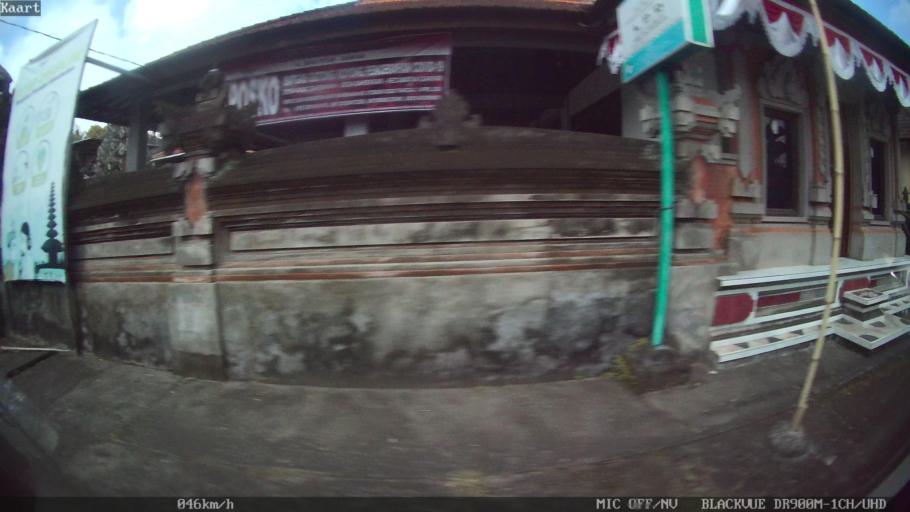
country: ID
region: Bali
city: Banjar Mulung
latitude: -8.5106
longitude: 115.3192
